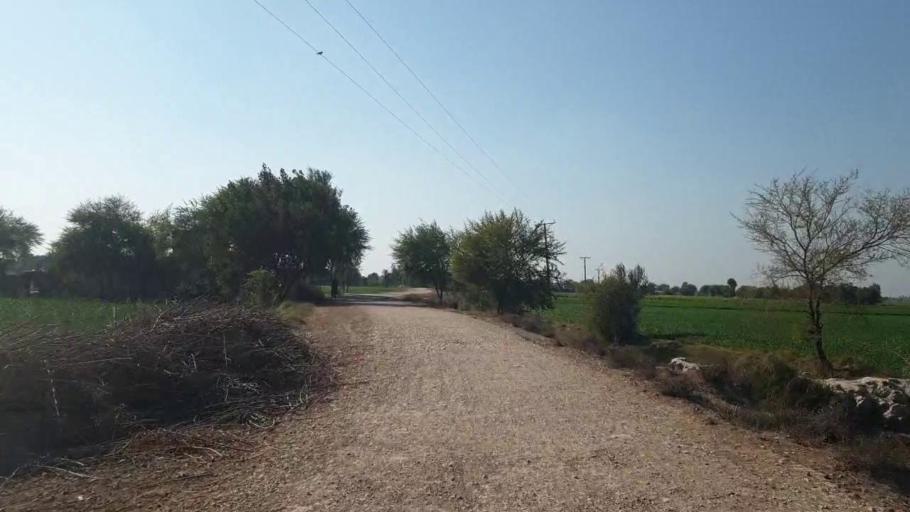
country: PK
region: Sindh
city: Shahdadpur
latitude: 25.9642
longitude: 68.6462
